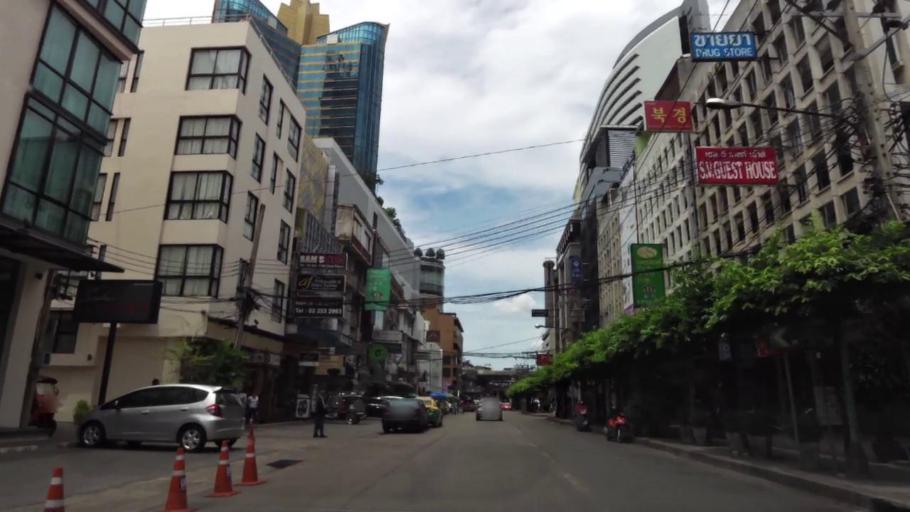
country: TH
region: Bangkok
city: Khlong Toei
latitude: 13.7395
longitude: 100.5601
